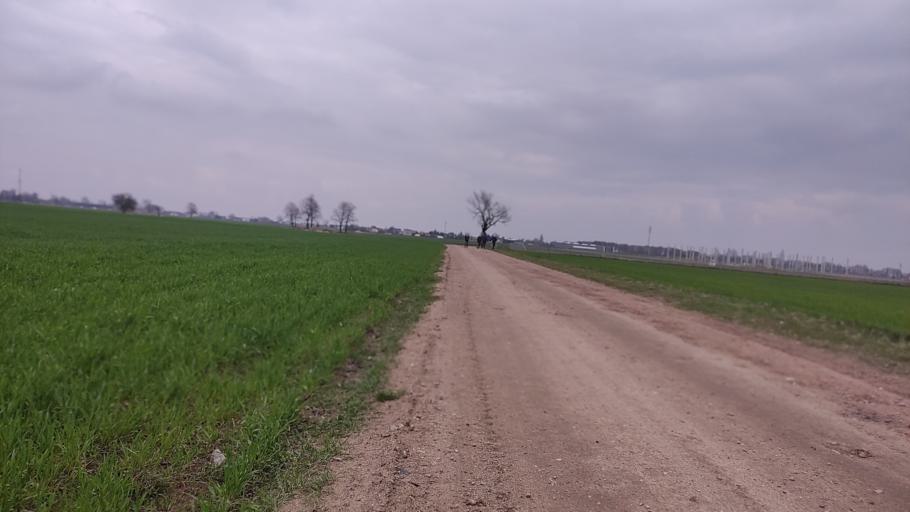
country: PL
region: Greater Poland Voivodeship
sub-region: Powiat poznanski
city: Swarzedz
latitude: 52.4050
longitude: 17.1418
